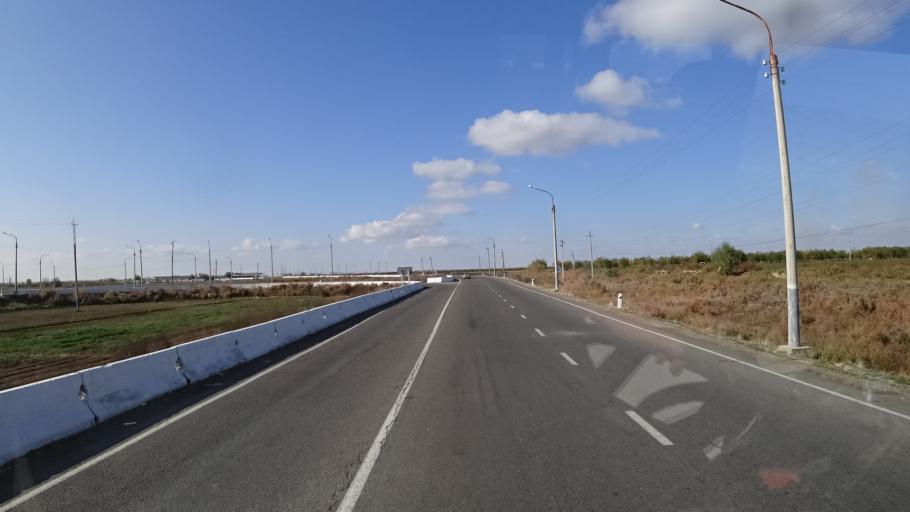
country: UZ
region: Sirdaryo
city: Guliston
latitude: 40.6263
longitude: 68.7217
